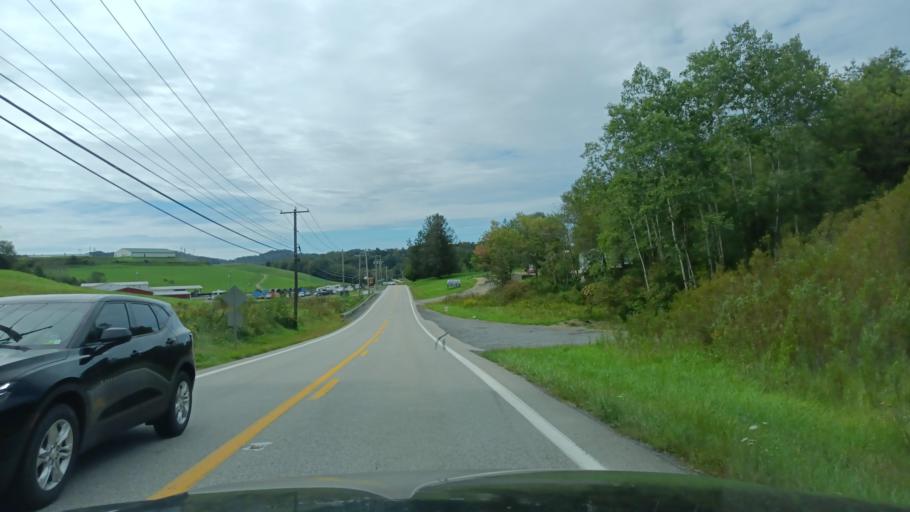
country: US
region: West Virginia
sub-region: Taylor County
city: Grafton
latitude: 39.3327
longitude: -80.0886
